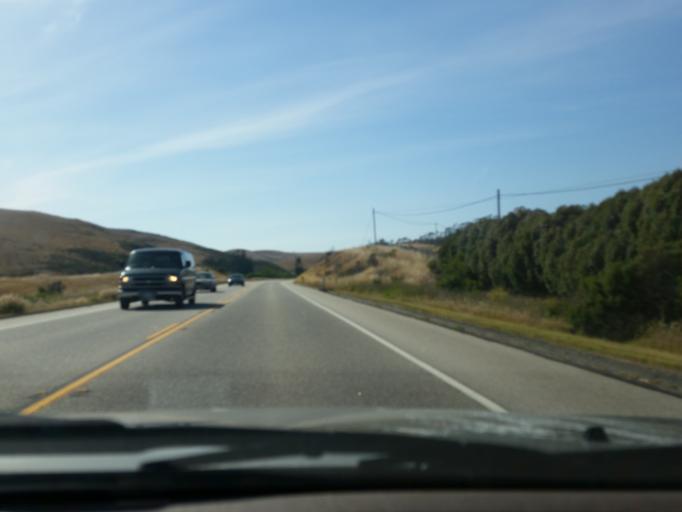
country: US
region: California
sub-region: San Luis Obispo County
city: Cayucos
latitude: 35.4646
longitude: -120.9710
